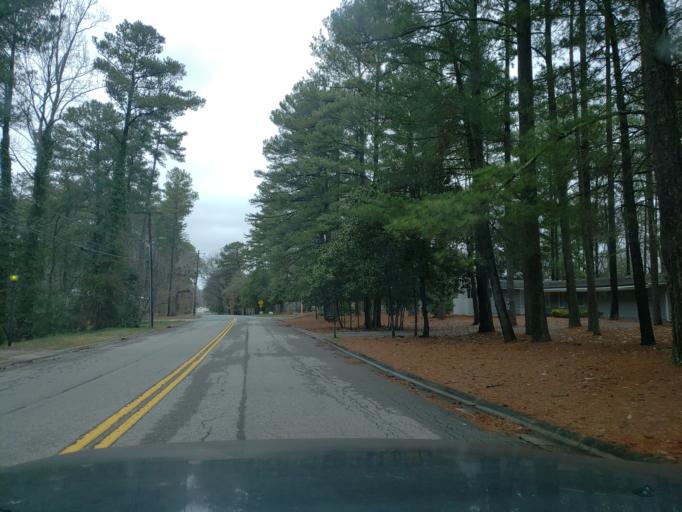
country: US
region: North Carolina
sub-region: Durham County
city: Durham
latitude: 35.9800
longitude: -78.9204
